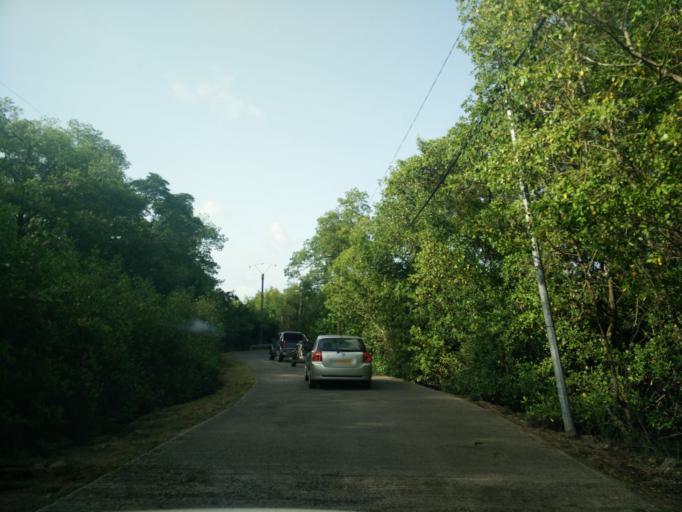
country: MQ
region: Martinique
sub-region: Martinique
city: Riviere-Pilote
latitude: 14.4676
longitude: -60.9088
